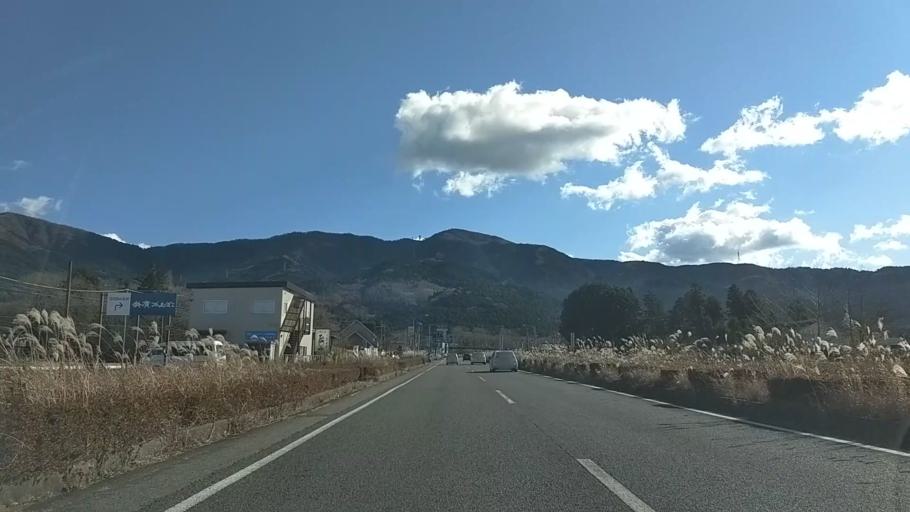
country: JP
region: Shizuoka
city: Gotemba
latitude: 35.2953
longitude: 138.9539
